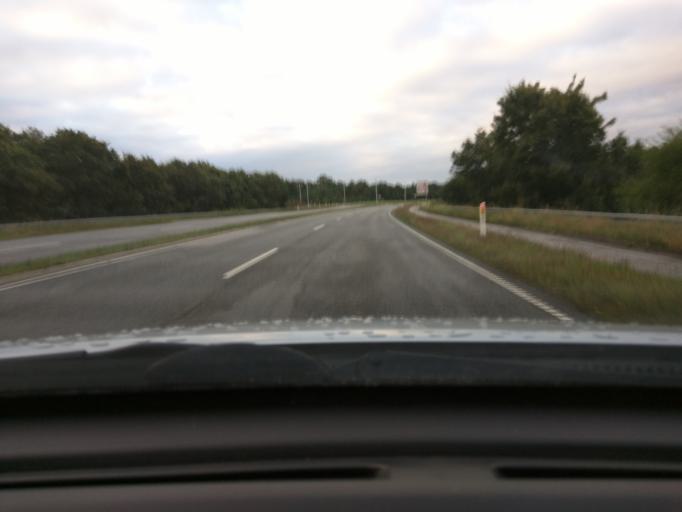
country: DK
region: Central Jutland
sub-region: Viborg Kommune
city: Viborg
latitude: 56.4286
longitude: 9.3900
